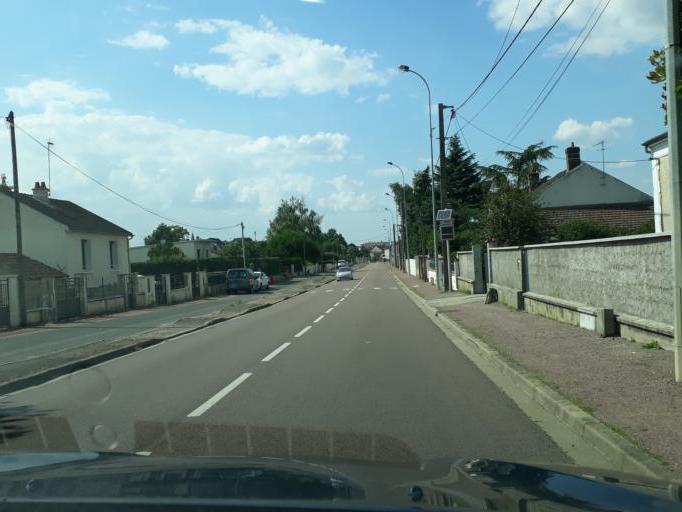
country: FR
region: Bourgogne
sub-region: Departement de la Nievre
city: Fourchambault
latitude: 47.0101
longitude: 3.0910
